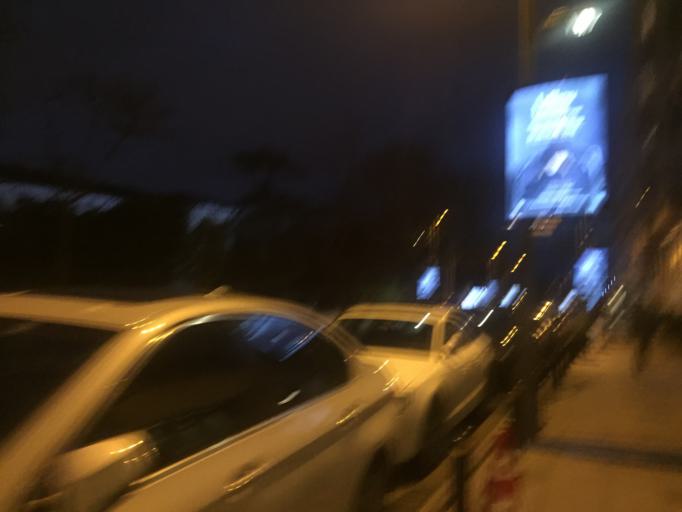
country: TR
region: Istanbul
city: Sisli
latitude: 41.0464
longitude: 28.9943
